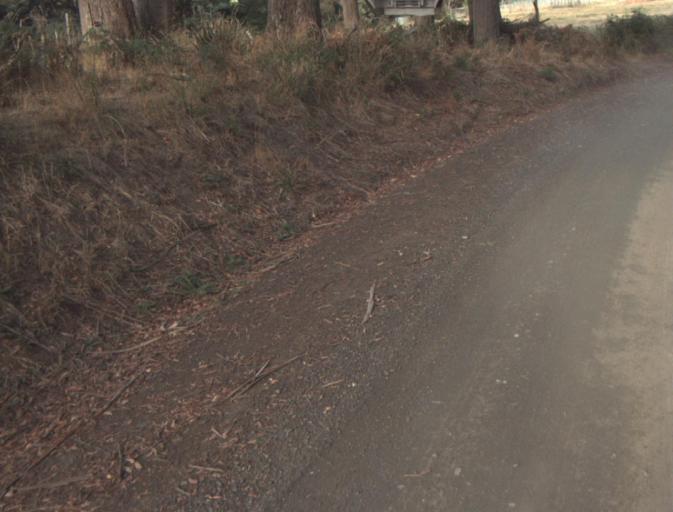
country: AU
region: Tasmania
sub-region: Launceston
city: Mayfield
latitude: -41.2706
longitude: 147.1755
